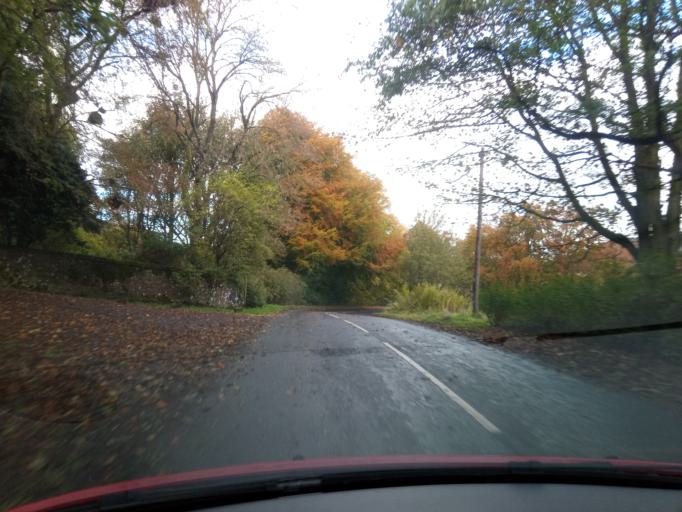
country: GB
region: Scotland
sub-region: The Scottish Borders
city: Newtown St Boswells
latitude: 55.5536
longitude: -2.7056
